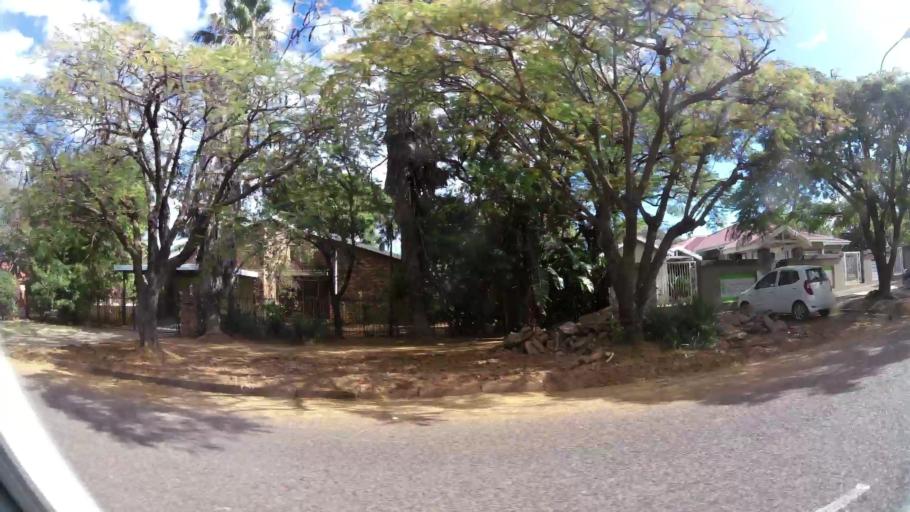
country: ZA
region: Limpopo
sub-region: Waterberg District Municipality
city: Warmbaths
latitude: -24.8796
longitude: 28.2880
